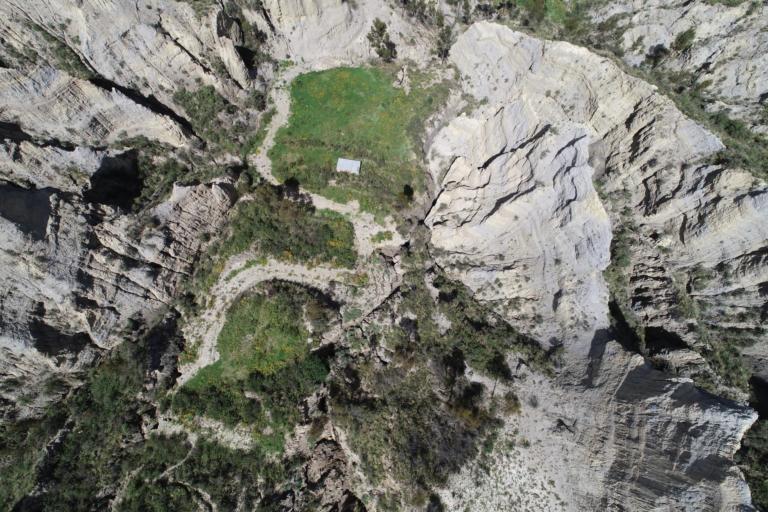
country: BO
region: La Paz
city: La Paz
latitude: -16.5007
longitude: -68.0640
